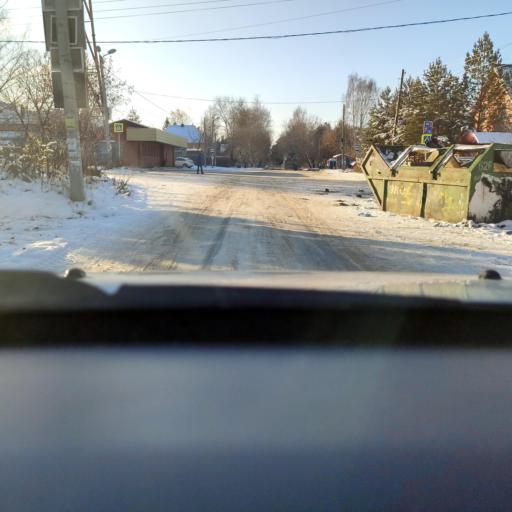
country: RU
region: Perm
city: Perm
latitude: 58.0545
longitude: 56.2970
